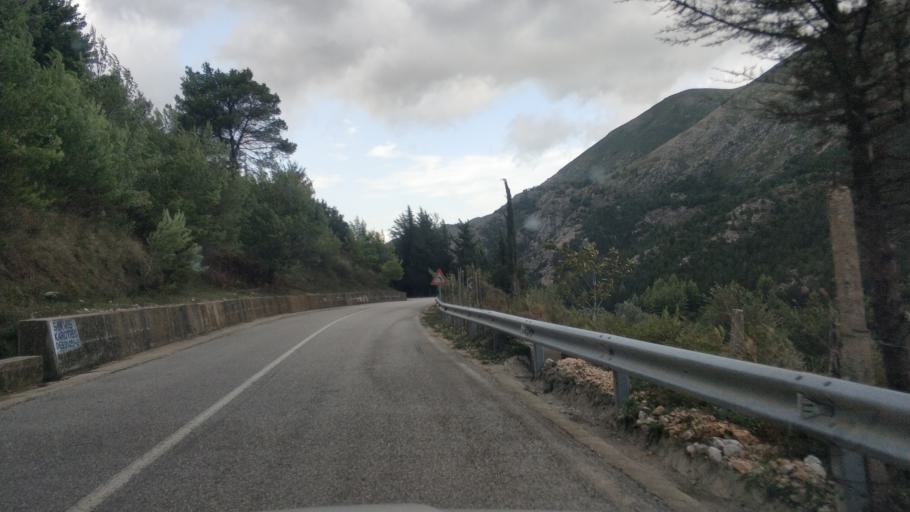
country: AL
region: Vlore
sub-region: Rrethi i Vlores
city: Orikum
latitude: 40.2448
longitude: 19.5502
